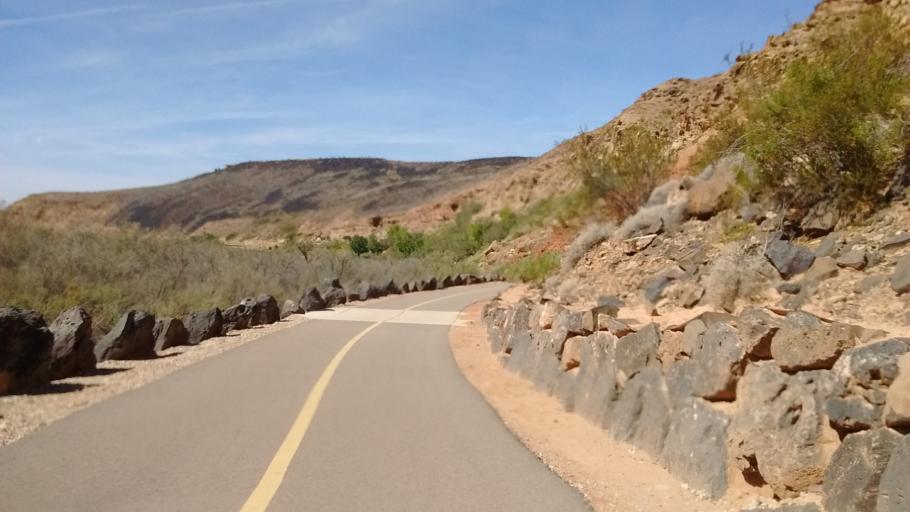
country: US
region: Utah
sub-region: Washington County
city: Washington
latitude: 37.1243
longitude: -113.4891
